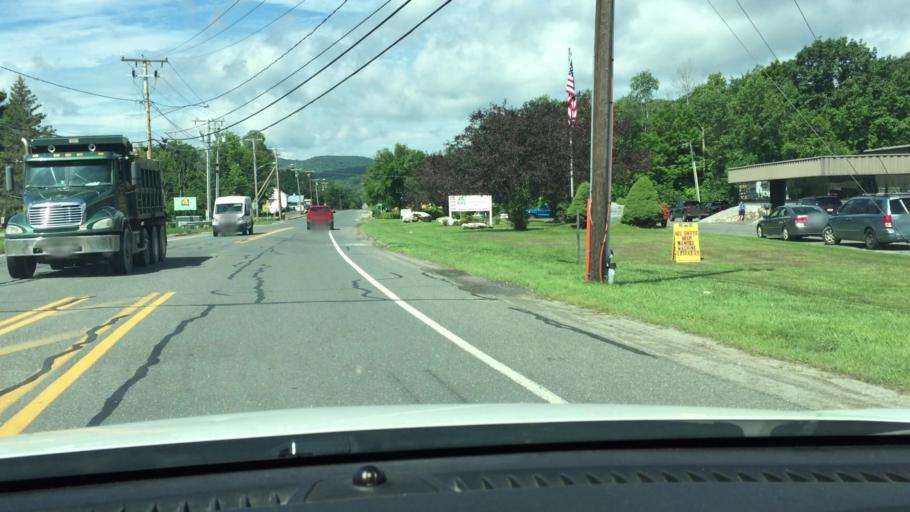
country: US
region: Massachusetts
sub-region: Berkshire County
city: Pittsfield
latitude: 42.4314
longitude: -73.3179
